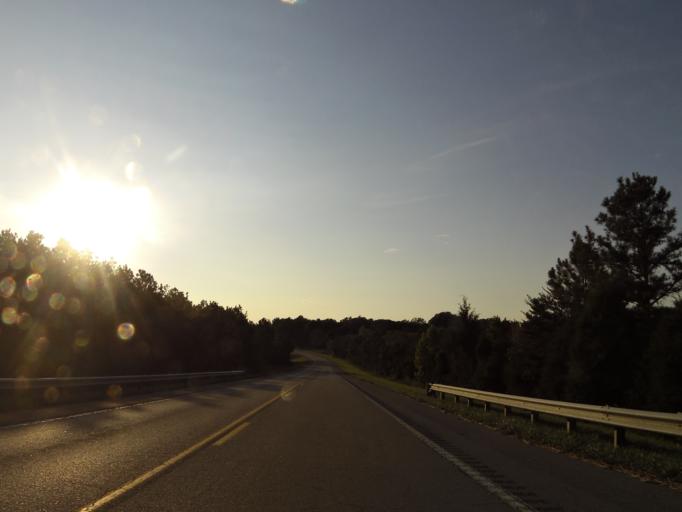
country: US
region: Tennessee
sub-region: McMinn County
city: Athens
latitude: 35.5188
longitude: -84.6344
